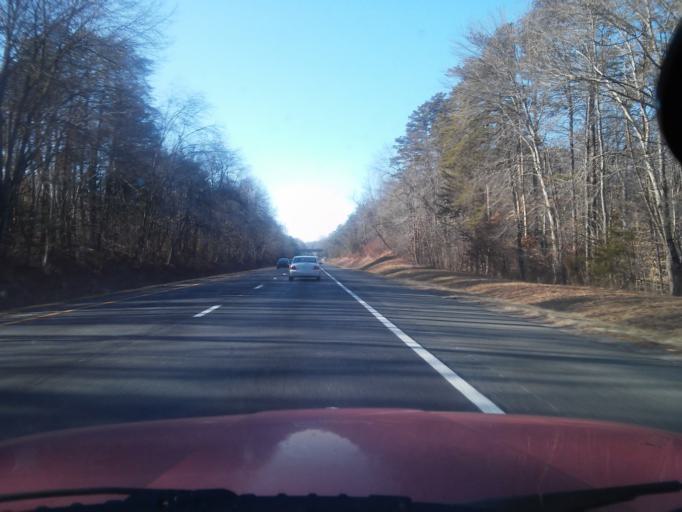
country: US
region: Virginia
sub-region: Fluvanna County
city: Lake Monticello
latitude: 38.0051
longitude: -78.3600
